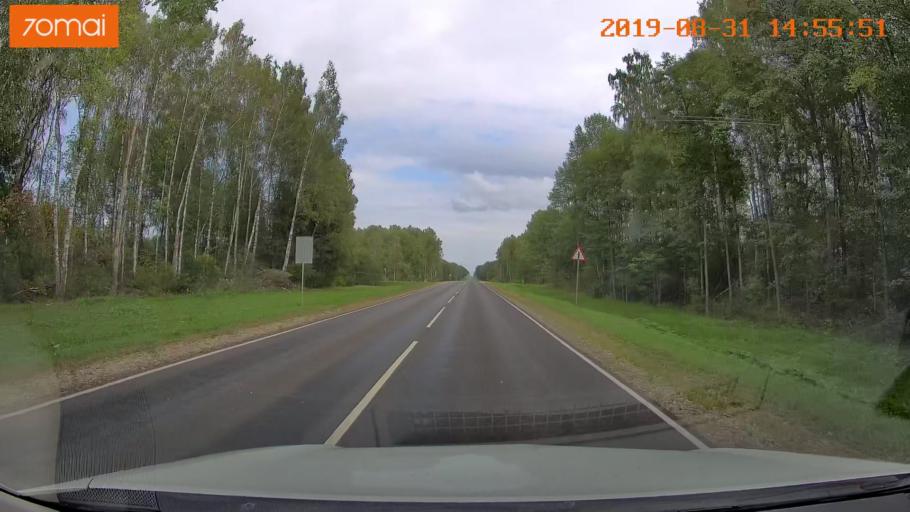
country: RU
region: Kaluga
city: Spas-Demensk
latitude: 54.3008
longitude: 33.9243
